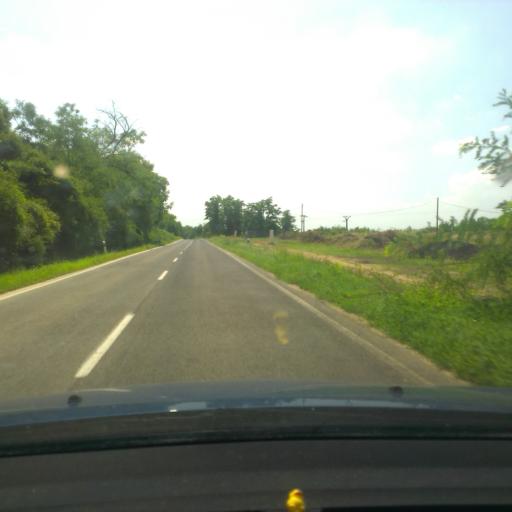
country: SK
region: Trnavsky
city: Hlohovec
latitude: 48.4841
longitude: 17.8085
